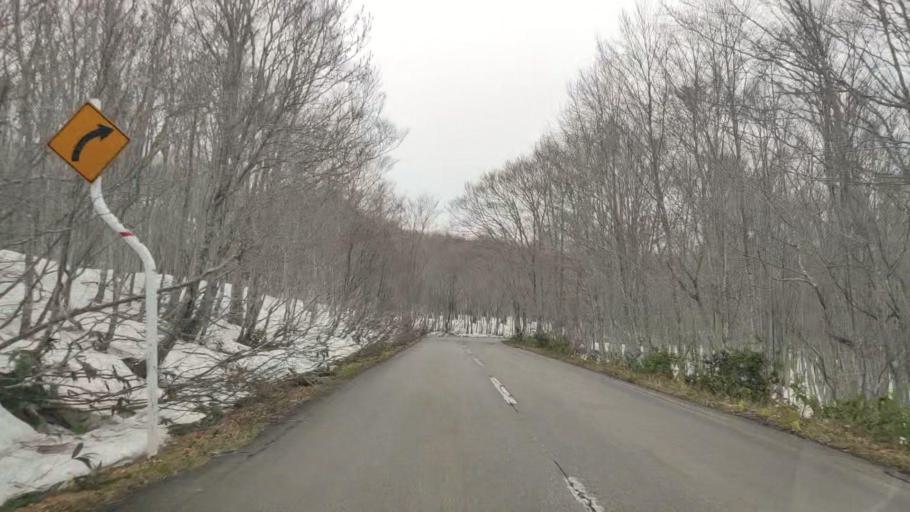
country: JP
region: Aomori
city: Aomori Shi
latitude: 40.6455
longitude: 140.9436
